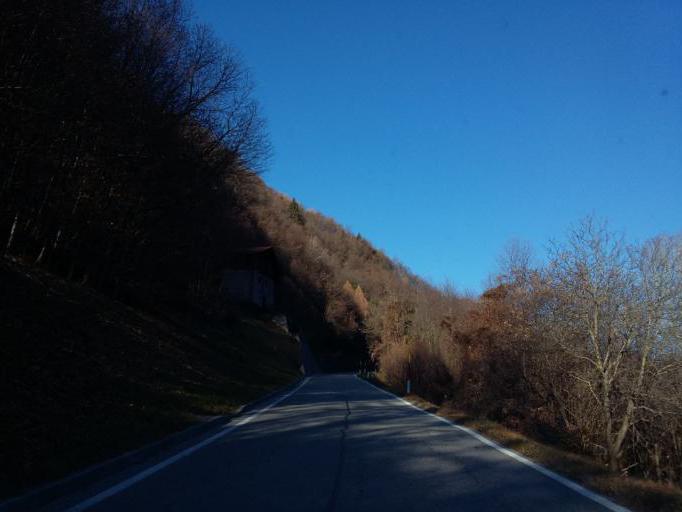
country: IT
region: Trentino-Alto Adige
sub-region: Provincia di Trento
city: Brione
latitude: 45.8958
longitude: 10.5967
